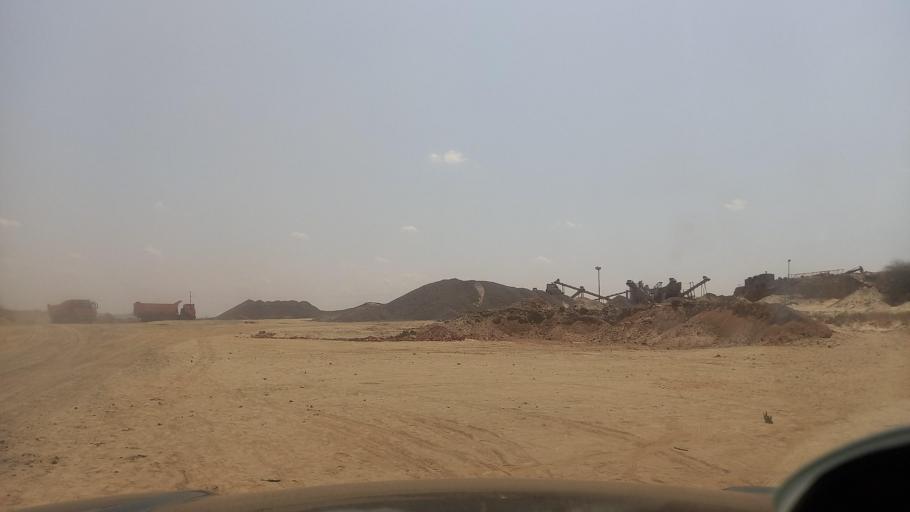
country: TZ
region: Dodoma
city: Msanga
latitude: -6.1800
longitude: 36.0693
